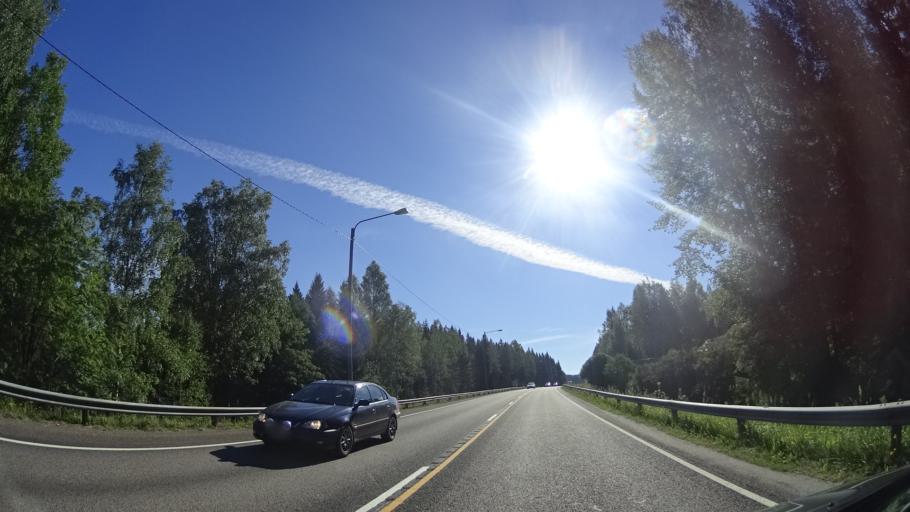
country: FI
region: Central Finland
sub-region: Jyvaeskylae
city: Petaejaevesi
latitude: 62.2716
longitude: 25.3221
